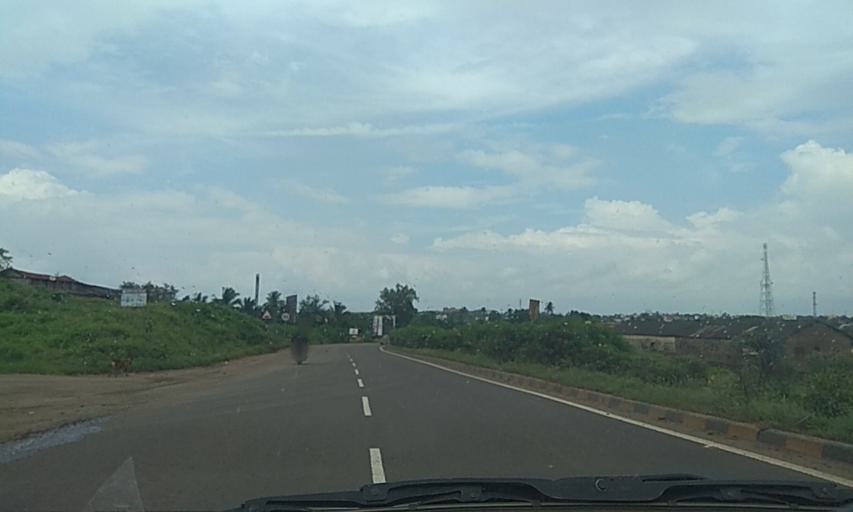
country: IN
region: Maharashtra
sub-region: Kolhapur
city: Kolhapur
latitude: 16.7875
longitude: 74.2788
